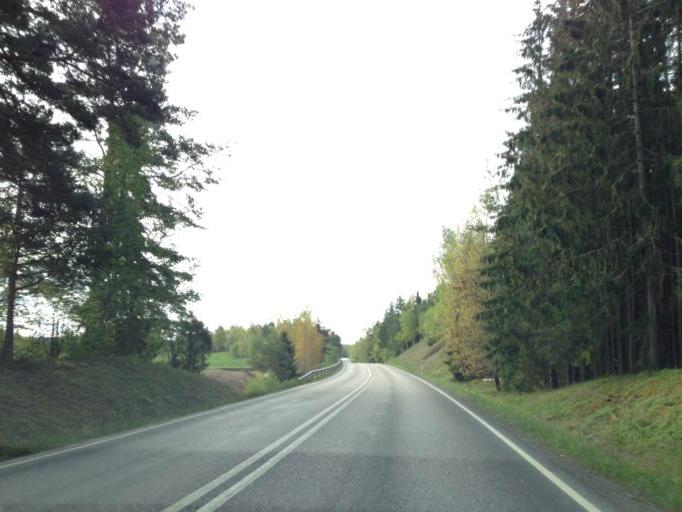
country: SE
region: Soedermanland
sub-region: Flens Kommun
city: Malmkoping
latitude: 59.0426
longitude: 16.8366
